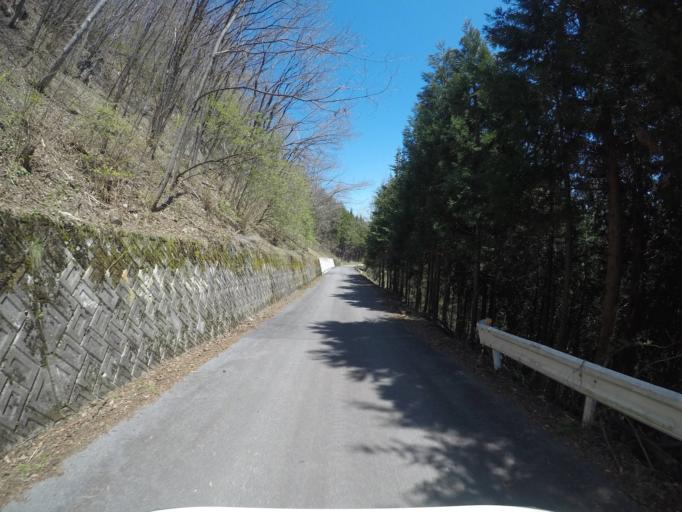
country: JP
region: Gifu
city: Takayama
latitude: 36.1542
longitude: 137.4288
